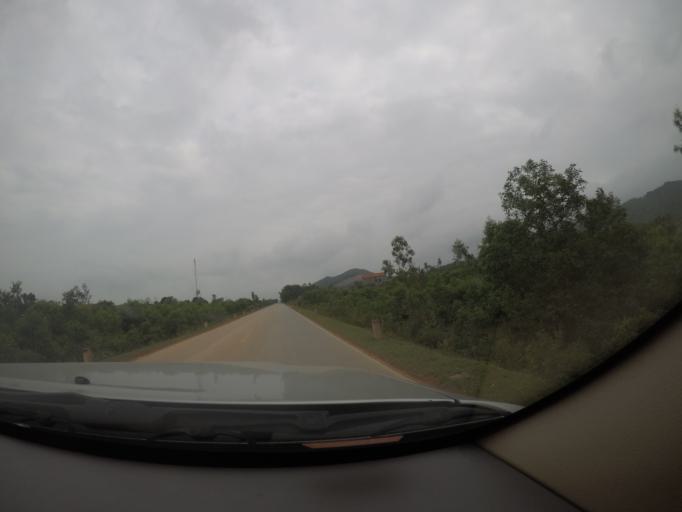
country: VN
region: Quang Binh
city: Quan Hau
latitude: 17.2824
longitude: 106.6503
